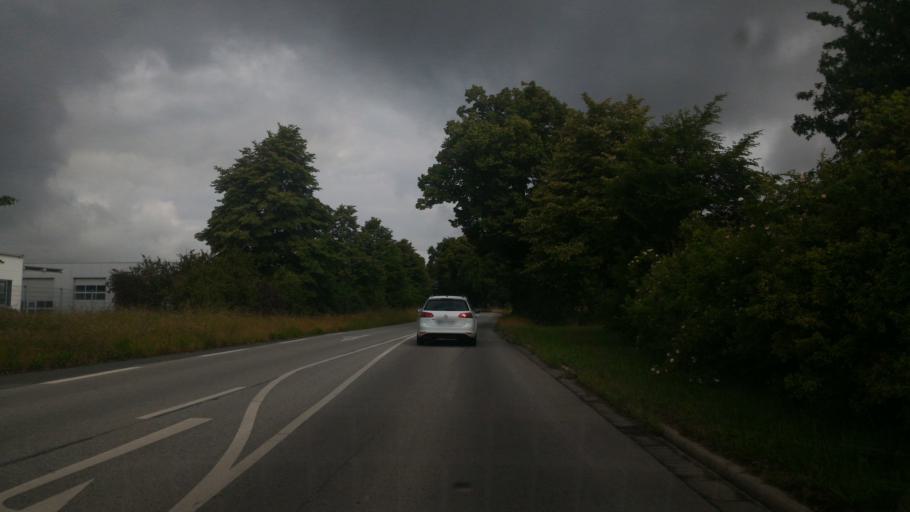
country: DE
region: Saxony
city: Neugersdorf
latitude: 50.9799
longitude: 14.6274
